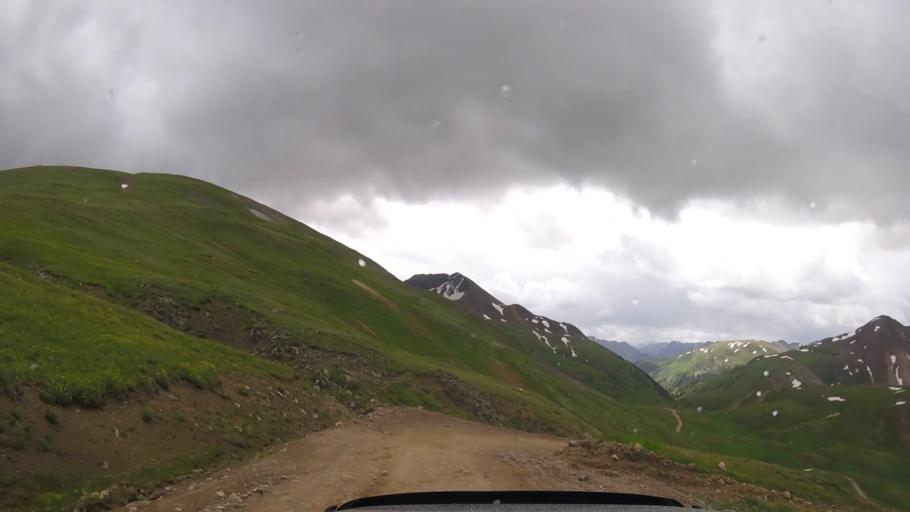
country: US
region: Colorado
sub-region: Ouray County
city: Ouray
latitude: 37.9620
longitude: -107.5758
